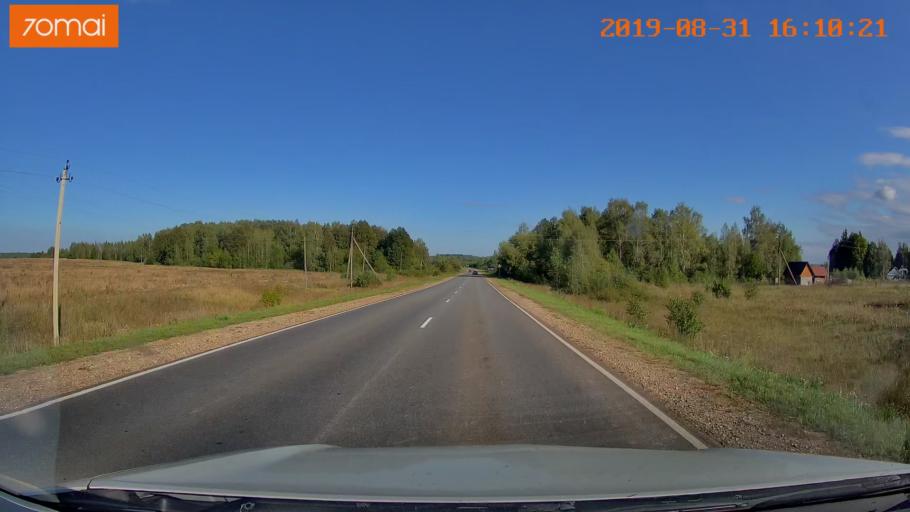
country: RU
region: Kaluga
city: Nikola-Lenivets
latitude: 54.5841
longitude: 35.4234
